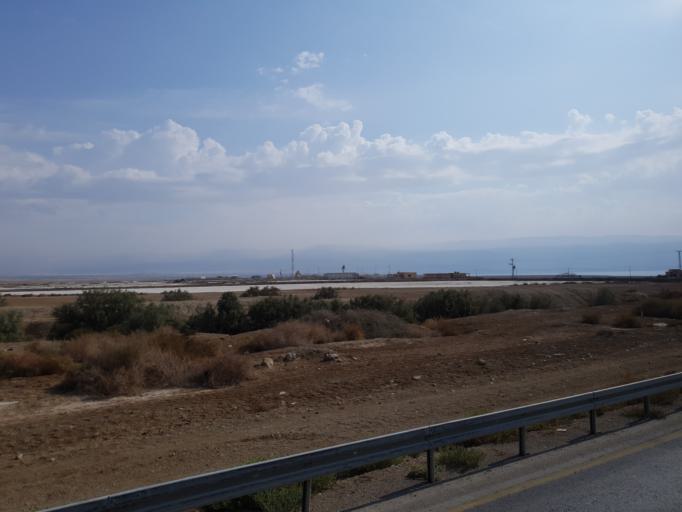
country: PS
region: West Bank
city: Jericho
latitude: 31.7756
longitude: 35.5045
